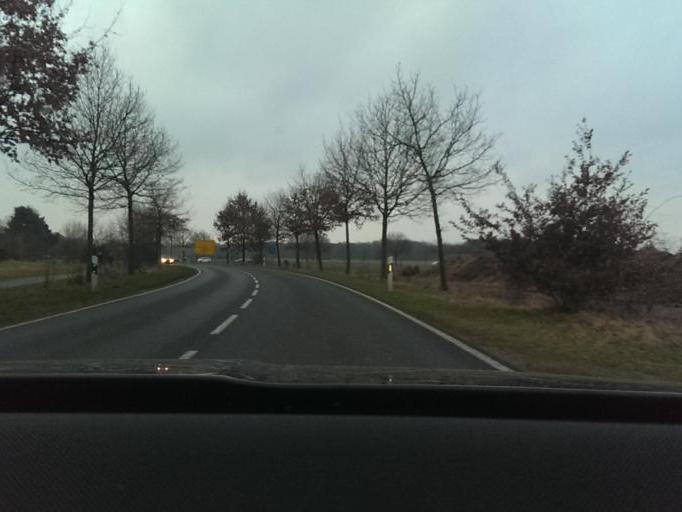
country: DE
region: Lower Saxony
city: Isernhagen Farster Bauerschaft
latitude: 52.4822
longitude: 9.8551
